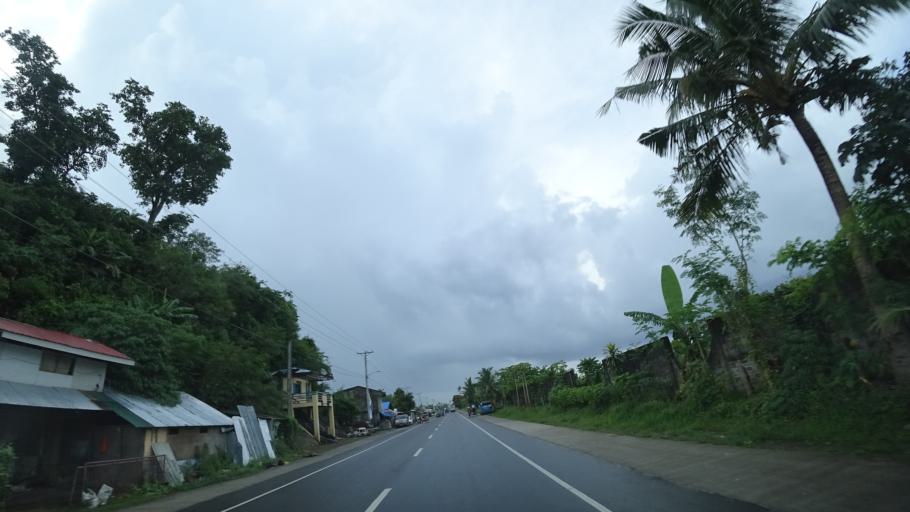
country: PH
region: Eastern Visayas
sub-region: Province of Leyte
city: Bislig
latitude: 11.0692
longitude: 125.0342
